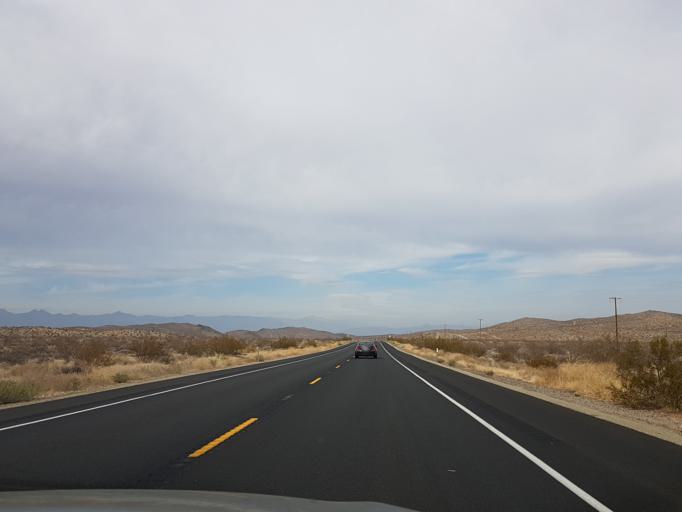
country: US
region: California
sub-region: Kern County
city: Ridgecrest
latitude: 35.5121
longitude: -117.6695
